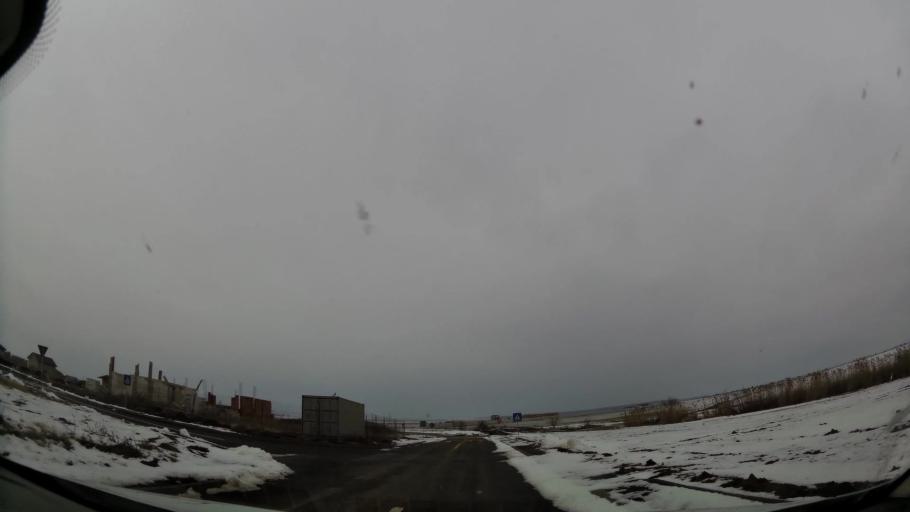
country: RO
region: Ilfov
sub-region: Comuna Tunari
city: Tunari
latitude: 44.5499
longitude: 26.1590
